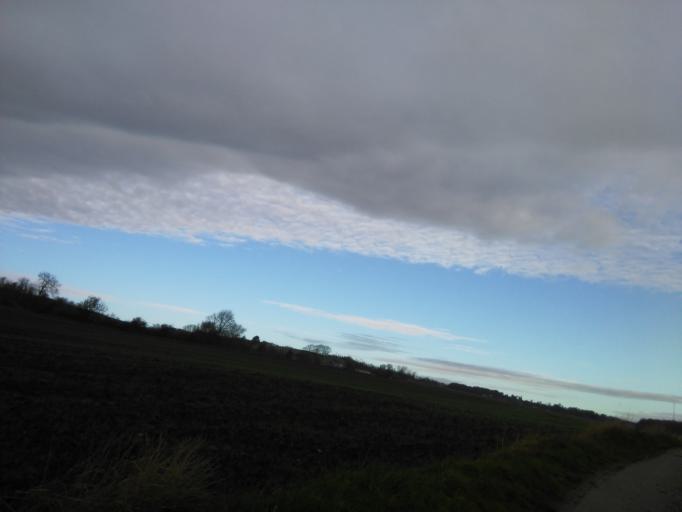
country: DK
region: Central Jutland
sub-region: Arhus Kommune
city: Marslet
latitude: 56.0795
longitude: 10.1814
